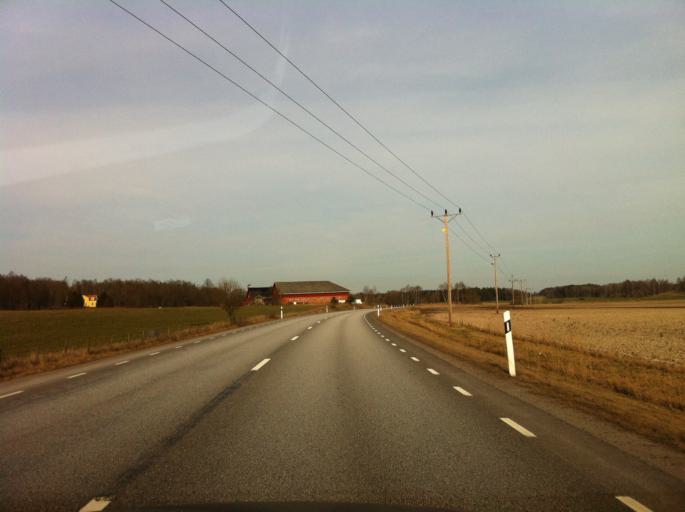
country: SE
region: Vaestra Goetaland
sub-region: Mariestads Kommun
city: Mariestad
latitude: 58.7658
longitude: 13.9501
